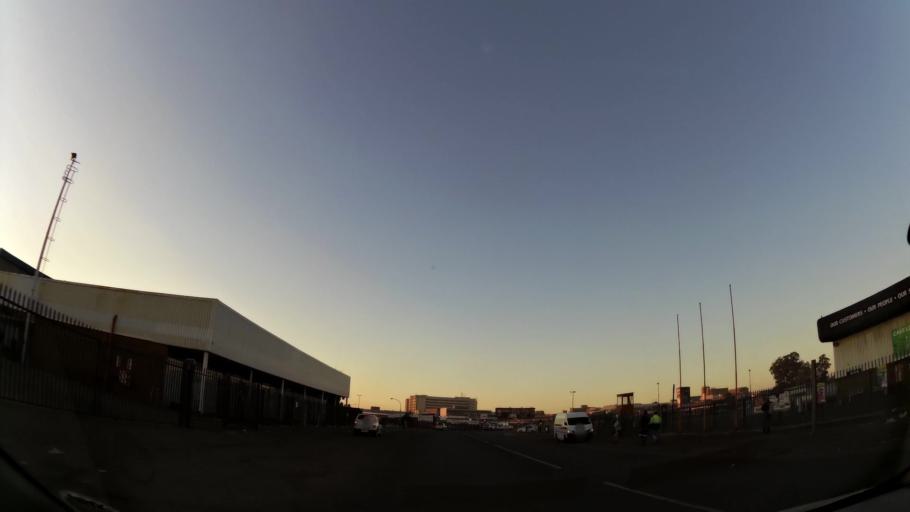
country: ZA
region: Mpumalanga
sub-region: Nkangala District Municipality
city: Witbank
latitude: -25.8783
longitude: 29.2082
